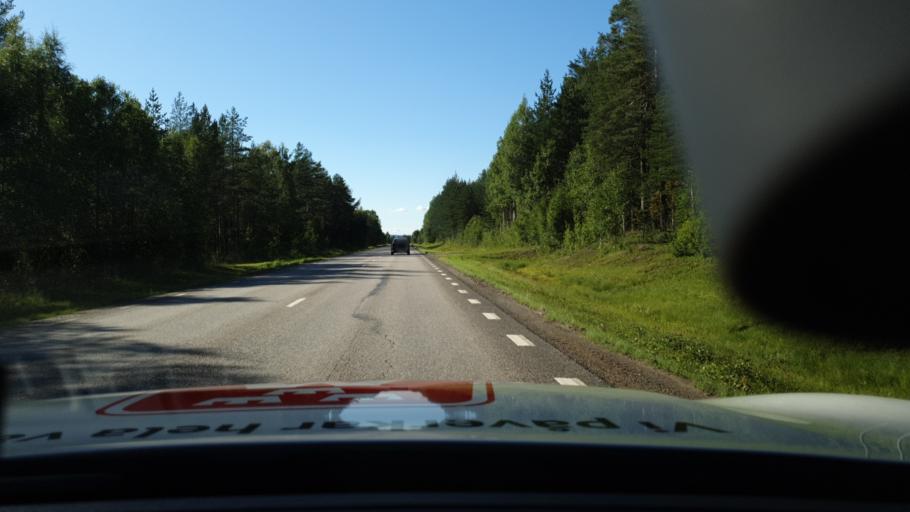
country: SE
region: Norrbotten
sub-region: Pitea Kommun
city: Rosvik
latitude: 65.5604
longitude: 21.7976
